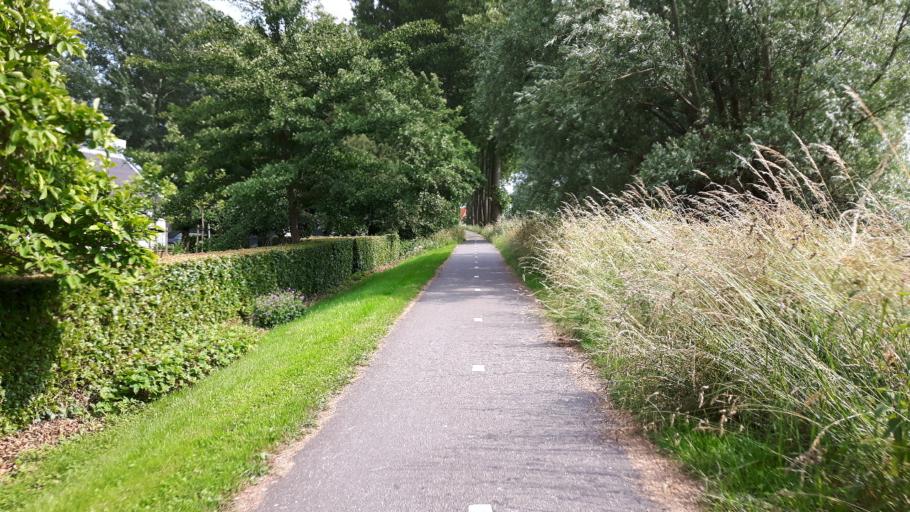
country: NL
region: Utrecht
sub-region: Stichtse Vecht
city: Spechtenkamp
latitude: 52.1144
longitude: 4.9768
